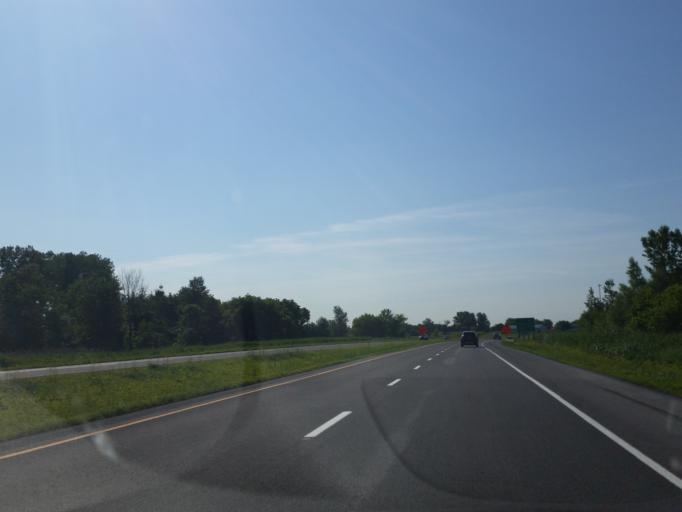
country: CA
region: Quebec
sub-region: Monteregie
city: Napierville
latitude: 45.2015
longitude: -73.4589
